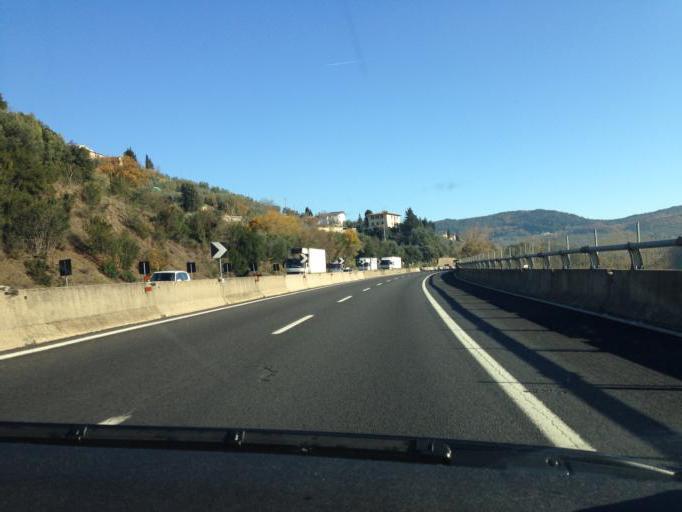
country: IT
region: Tuscany
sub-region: Province of Florence
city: Antella
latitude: 43.7288
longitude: 11.3519
